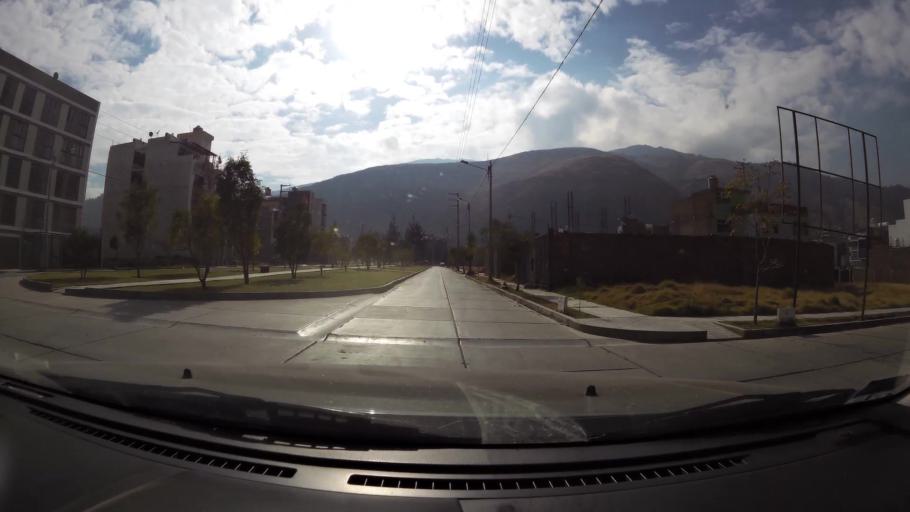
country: PE
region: Junin
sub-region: Provincia de Huancayo
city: Huancayo
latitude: -12.0489
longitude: -75.1907
